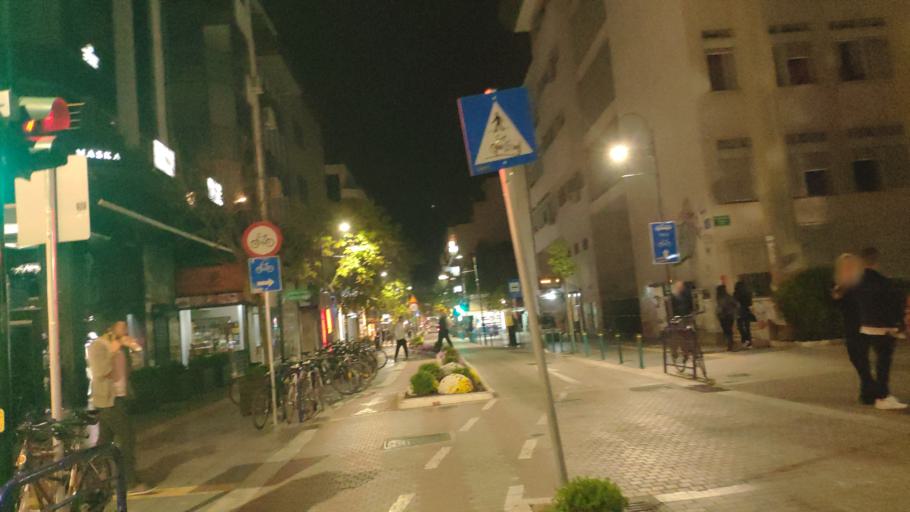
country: GR
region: Thessaly
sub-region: Nomos Larisis
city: Larisa
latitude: 39.6378
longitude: 22.4167
